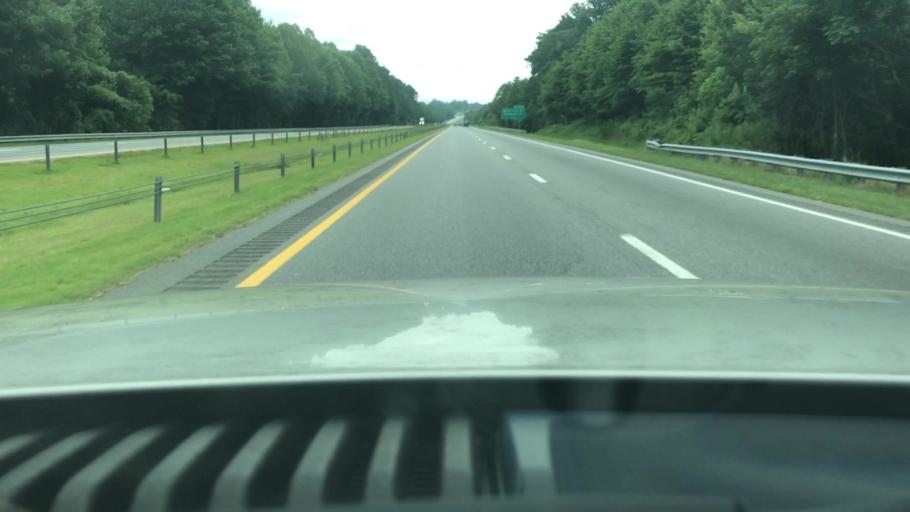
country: US
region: North Carolina
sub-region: Wilkes County
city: North Wilkesboro
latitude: 36.1474
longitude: -81.0403
